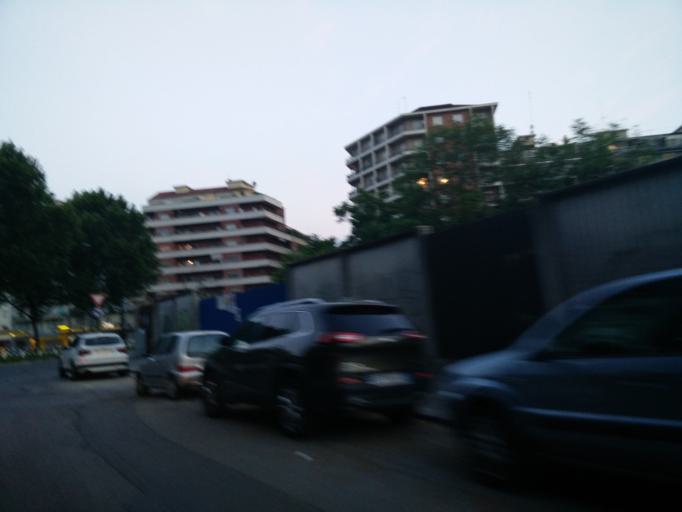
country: IT
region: Piedmont
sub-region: Provincia di Torino
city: Lesna
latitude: 45.0529
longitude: 7.6502
